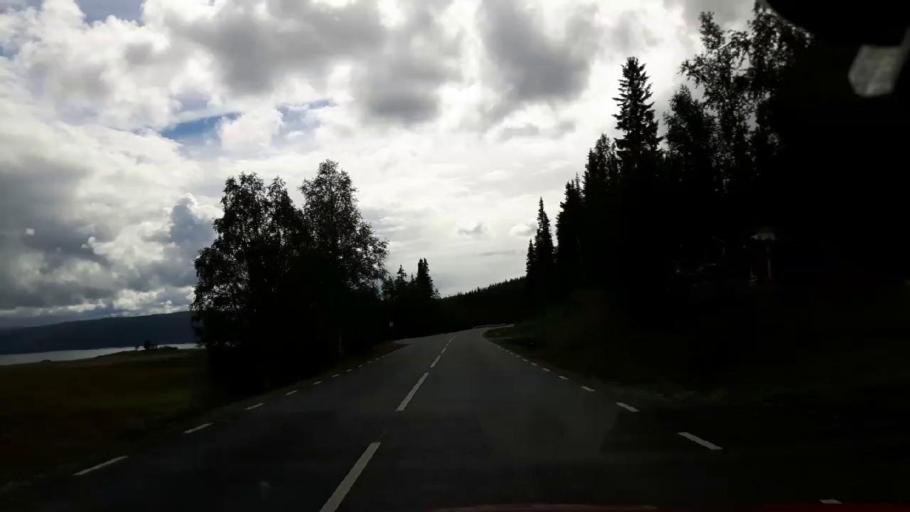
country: NO
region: Nord-Trondelag
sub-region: Royrvik
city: Royrvik
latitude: 64.8189
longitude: 14.0613
